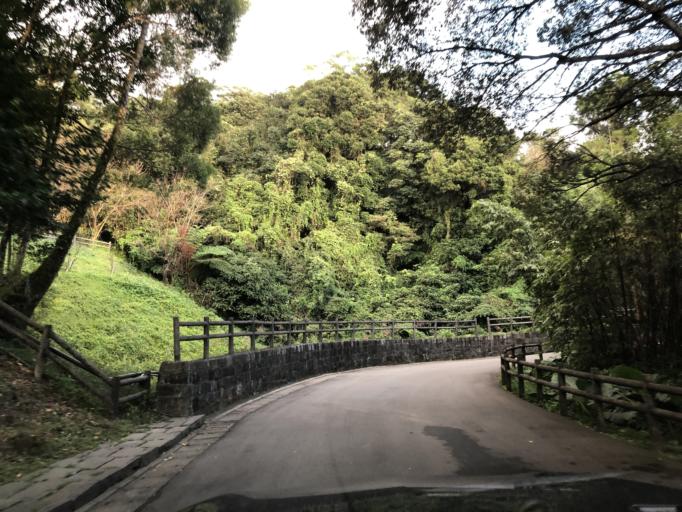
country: TW
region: Taipei
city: Taipei
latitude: 25.1525
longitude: 121.5583
